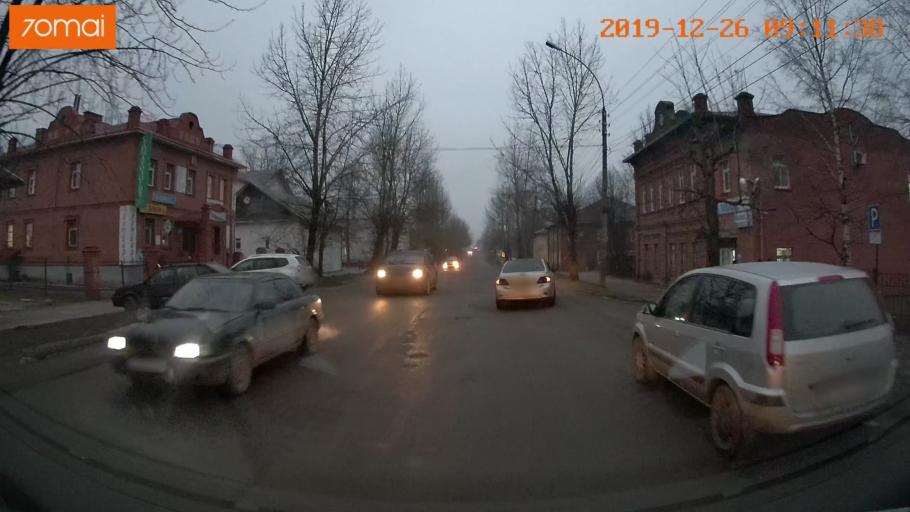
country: RU
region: Vologda
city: Gryazovets
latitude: 58.8772
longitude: 40.2528
